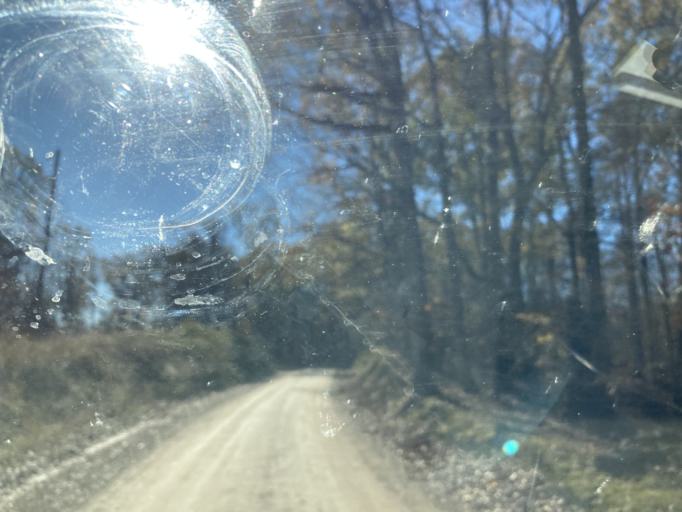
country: US
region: Mississippi
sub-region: Madison County
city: Kearney Park
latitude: 32.6682
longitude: -90.5099
